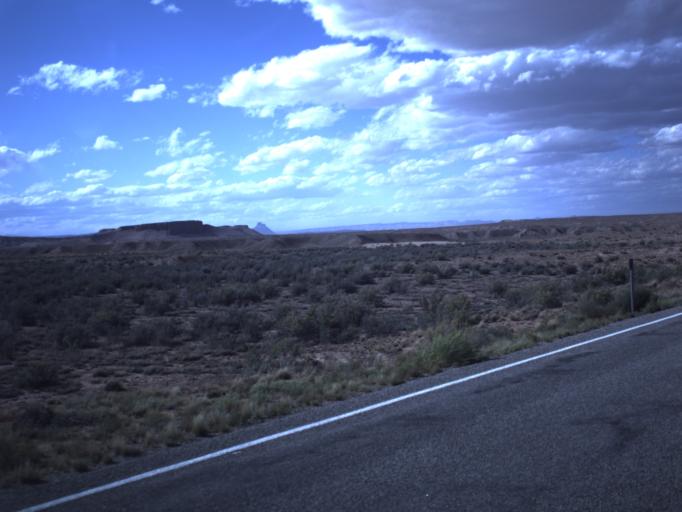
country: US
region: Utah
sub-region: Emery County
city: Ferron
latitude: 38.3124
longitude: -110.6728
